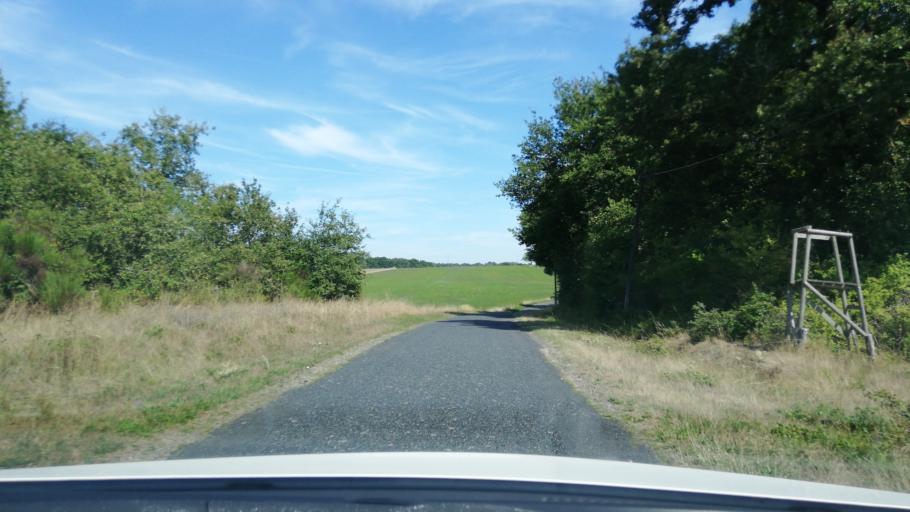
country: FR
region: Centre
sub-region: Departement d'Indre-et-Loire
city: Mazieres-de-Touraine
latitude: 47.3905
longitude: 0.4297
